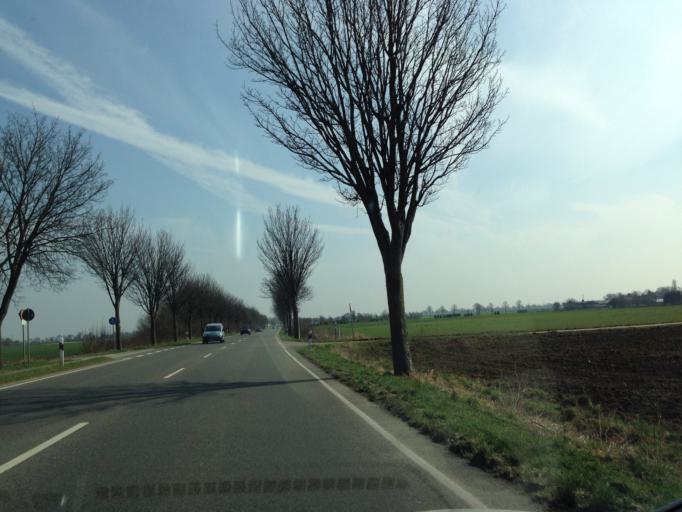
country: DE
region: North Rhine-Westphalia
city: Huckelhoven
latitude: 51.0926
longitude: 6.2535
